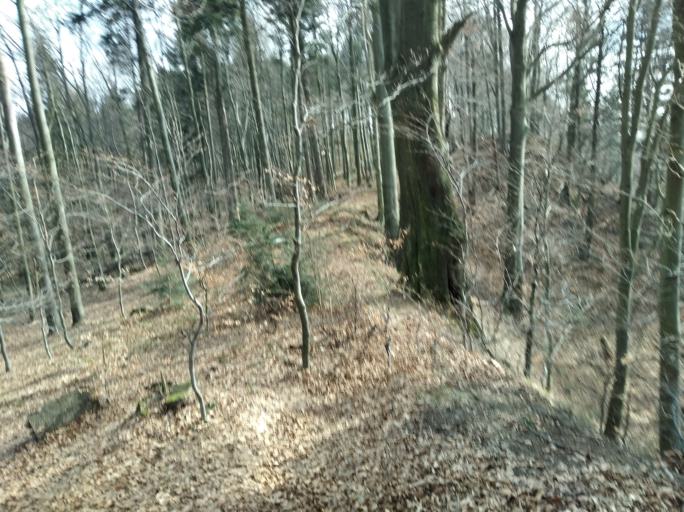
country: PL
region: Subcarpathian Voivodeship
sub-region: Powiat krosnienski
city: Korczyna
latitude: 49.7772
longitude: 21.8050
